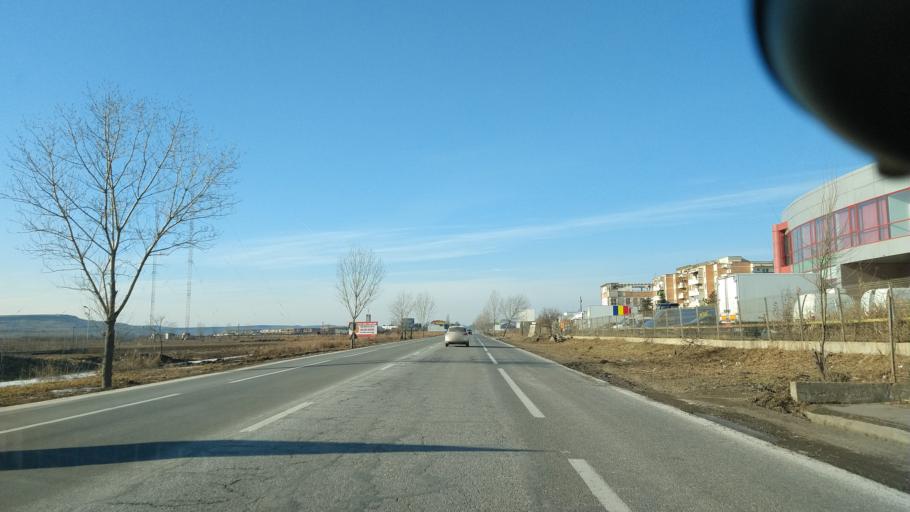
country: RO
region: Iasi
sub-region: Comuna Valea Lupului
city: Valea Lupului
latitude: 47.1827
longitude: 27.4650
